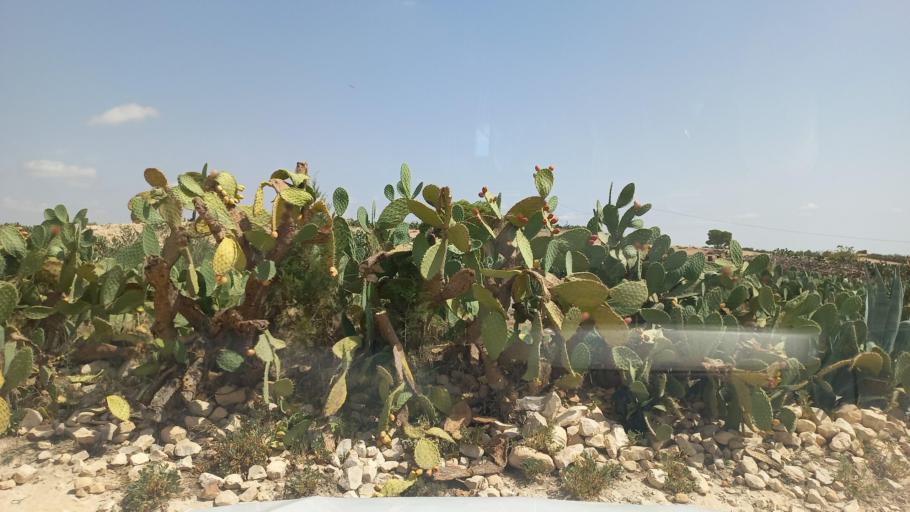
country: TN
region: Al Qasrayn
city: Sbiba
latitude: 35.4046
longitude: 8.9737
